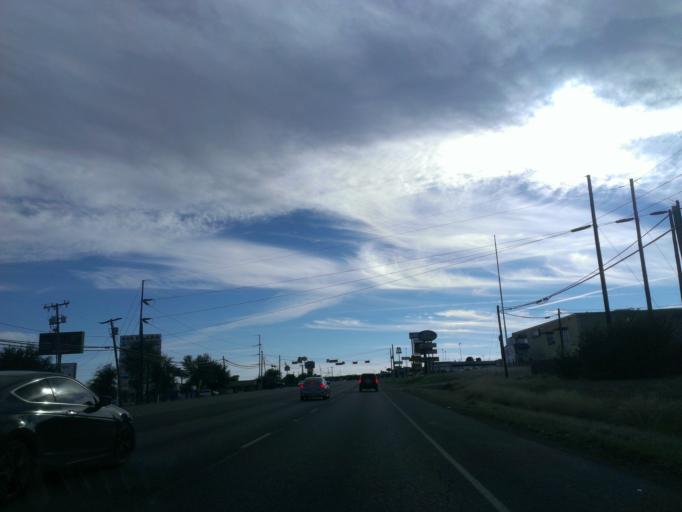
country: US
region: Texas
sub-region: Bell County
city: Killeen
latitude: 31.1142
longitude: -97.7457
